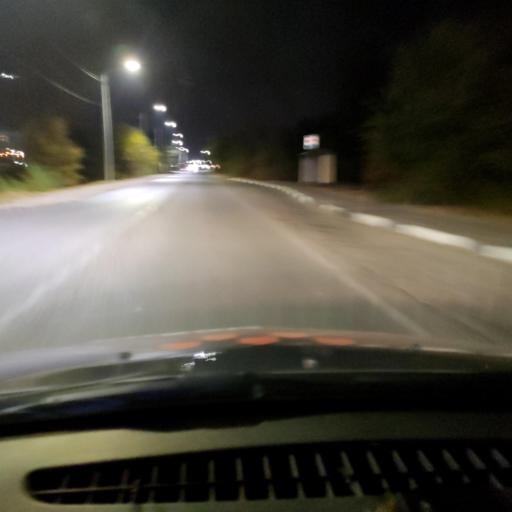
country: RU
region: Voronezj
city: Maslovka
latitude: 51.5869
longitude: 39.2480
